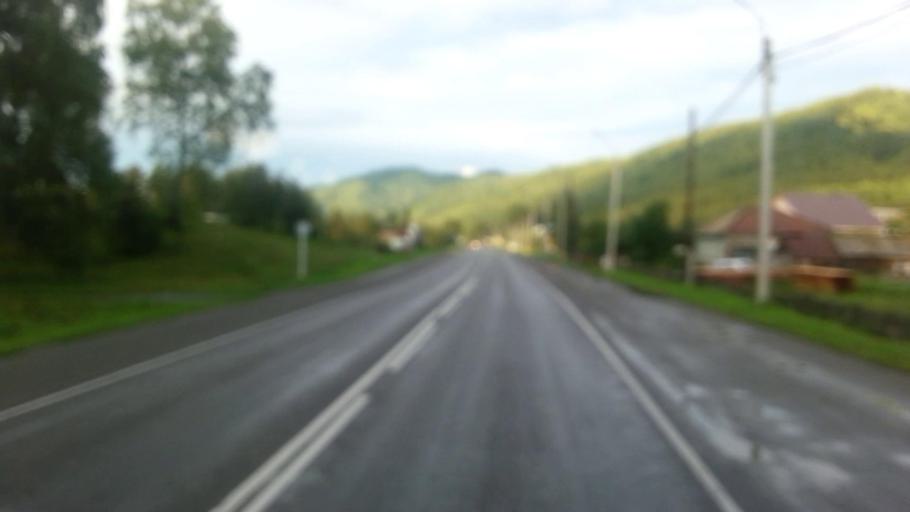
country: RU
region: Altay
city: Souzga
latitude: 51.8845
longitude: 85.8508
